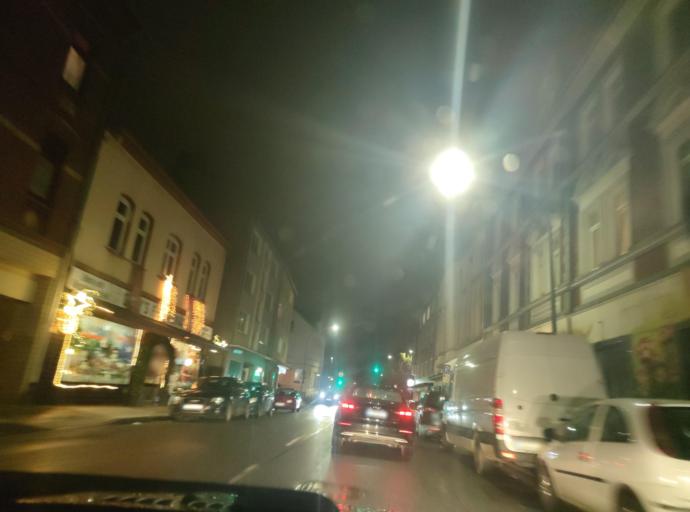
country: DE
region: North Rhine-Westphalia
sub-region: Regierungsbezirk Dusseldorf
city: Essen
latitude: 51.4873
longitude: 7.0644
